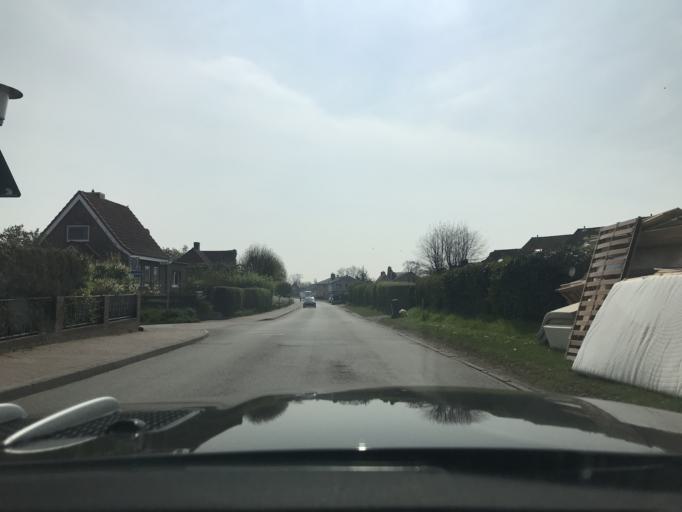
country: DE
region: Schleswig-Holstein
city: Gromitz
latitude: 54.1683
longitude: 10.9786
